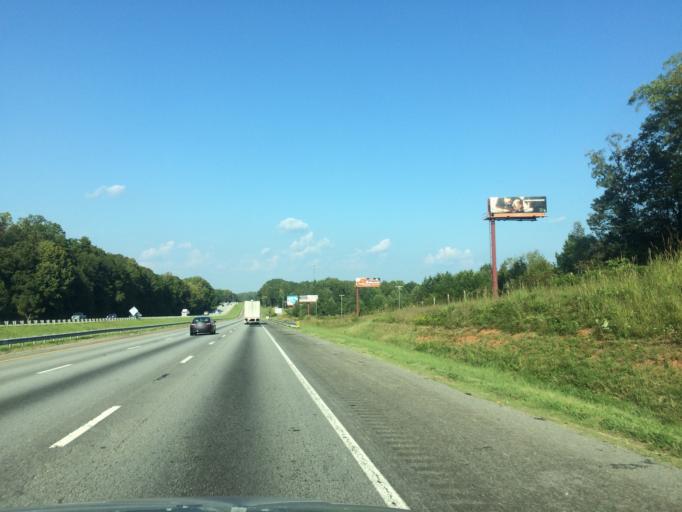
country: US
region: South Carolina
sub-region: Anderson County
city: Northlake
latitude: 34.5876
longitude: -82.6763
